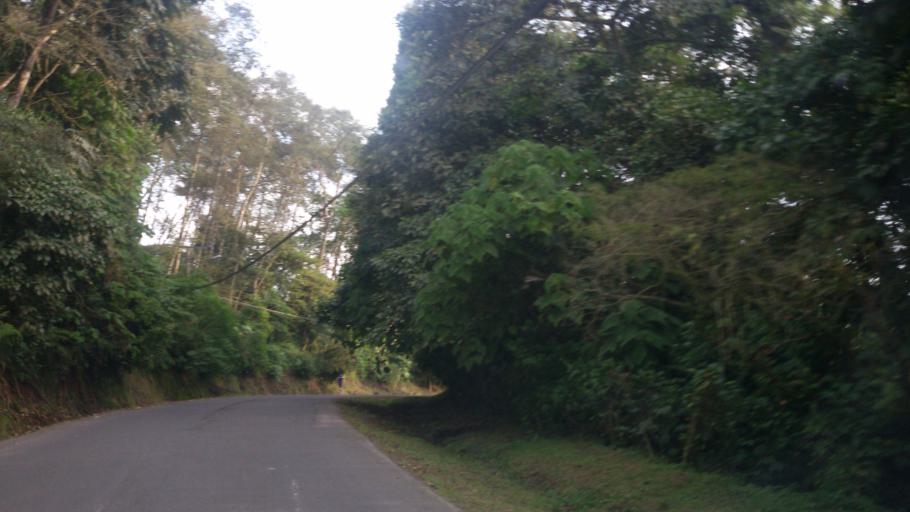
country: CR
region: San Jose
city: Ipis
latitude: 9.9940
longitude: -83.9602
